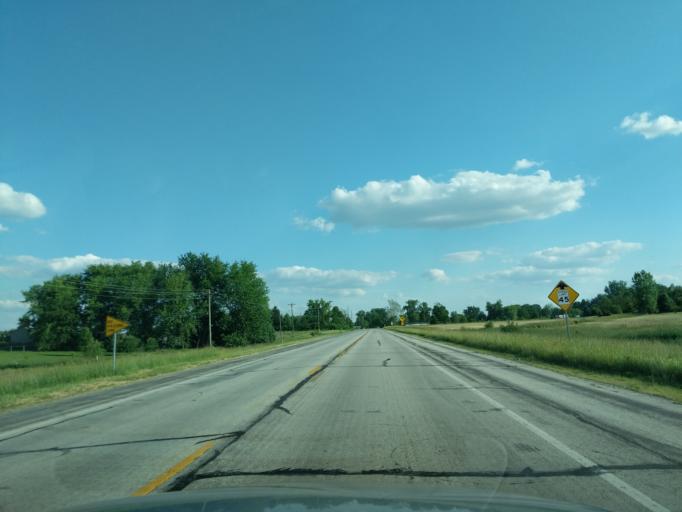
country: US
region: Indiana
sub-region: Whitley County
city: Tri-Lakes
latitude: 41.2878
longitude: -85.5007
